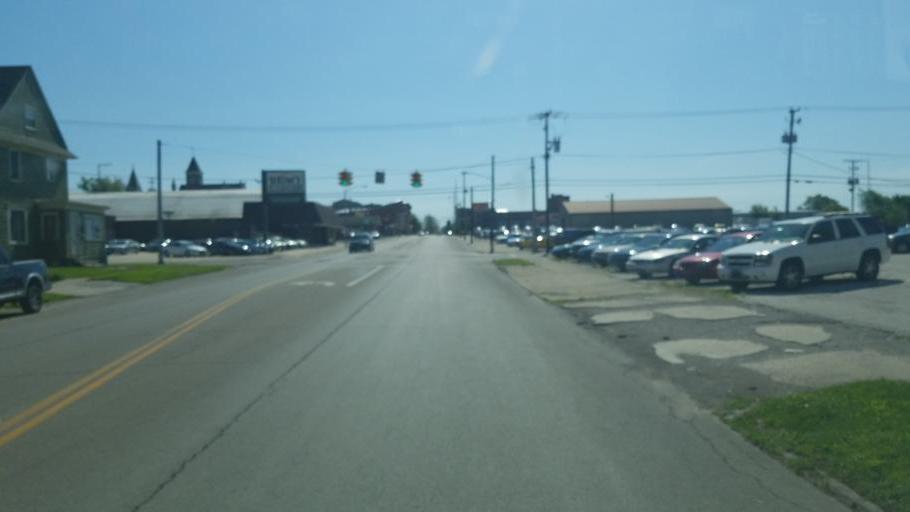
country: US
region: Ohio
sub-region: Hardin County
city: Kenton
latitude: 40.6473
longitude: -83.6141
